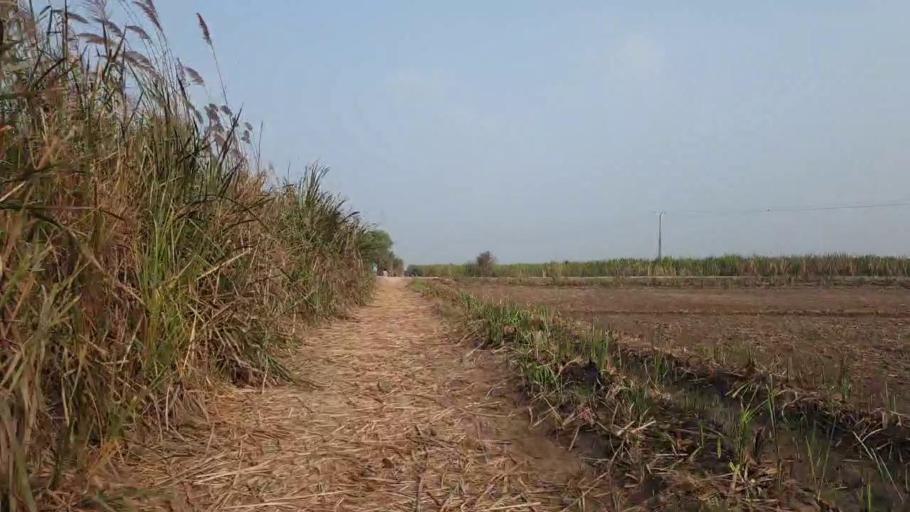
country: PK
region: Sindh
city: Tando Muhammad Khan
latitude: 25.1440
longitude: 68.5906
